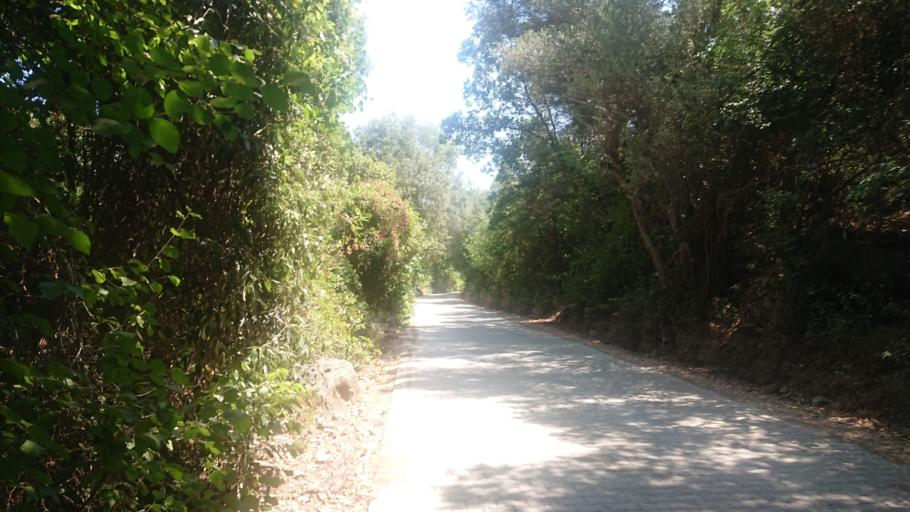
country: TR
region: Aydin
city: Atburgazi
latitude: 37.6981
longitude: 27.1734
